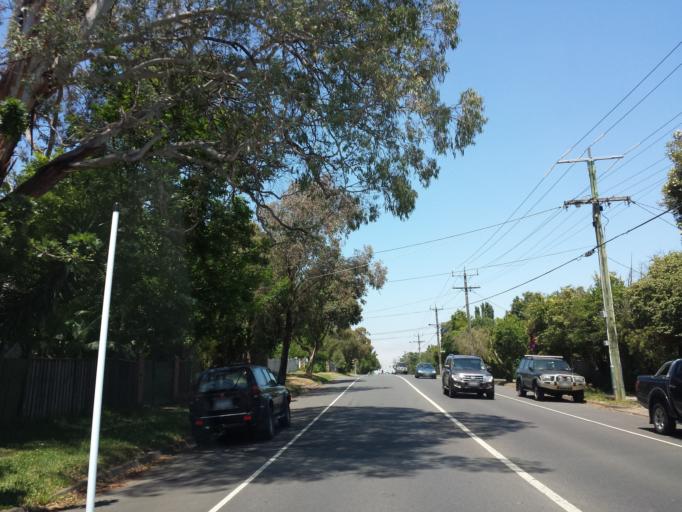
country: AU
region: Victoria
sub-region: Maroondah
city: Croydon North
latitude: -37.7932
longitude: 145.2912
